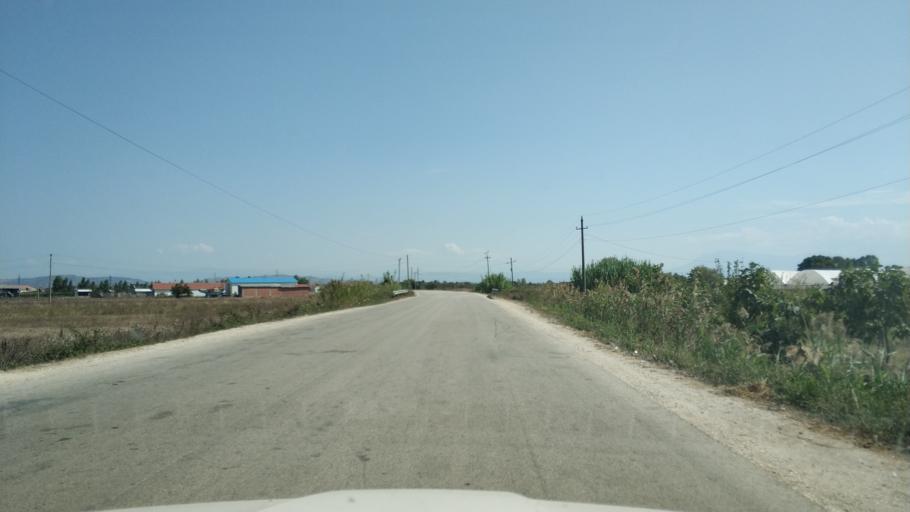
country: AL
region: Fier
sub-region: Rrethi i Lushnjes
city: Gradishte
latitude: 40.8837
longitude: 19.5838
